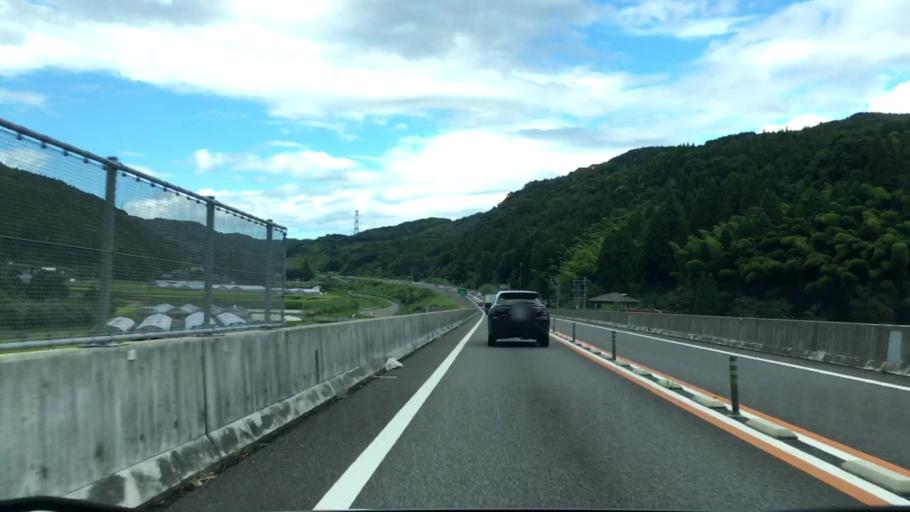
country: JP
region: Saga Prefecture
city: Karatsu
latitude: 33.3752
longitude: 129.9314
